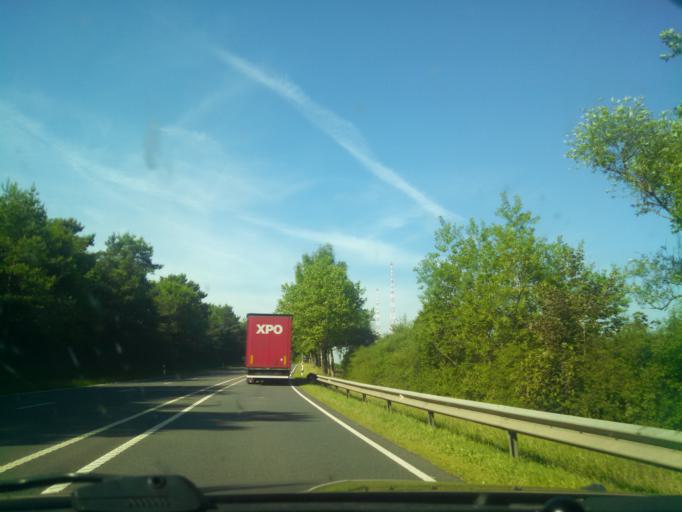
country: LU
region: Grevenmacher
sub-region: Canton de Grevenmacher
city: Junglinster
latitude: 49.7264
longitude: 6.2787
